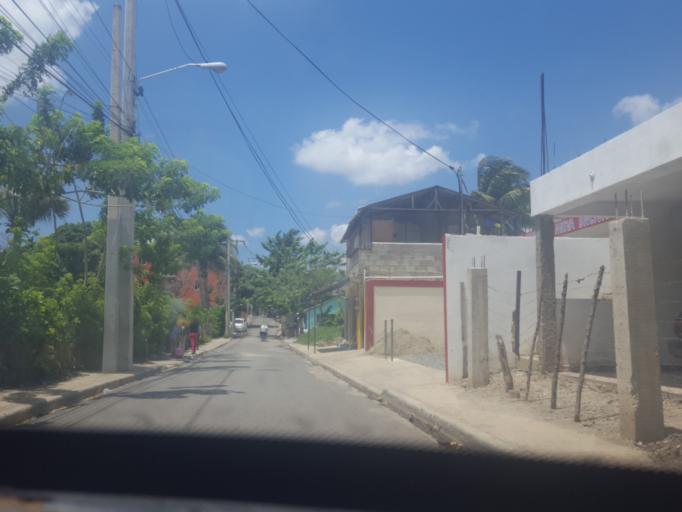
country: DO
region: Santiago
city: Santiago de los Caballeros
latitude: 19.4885
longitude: -70.6961
